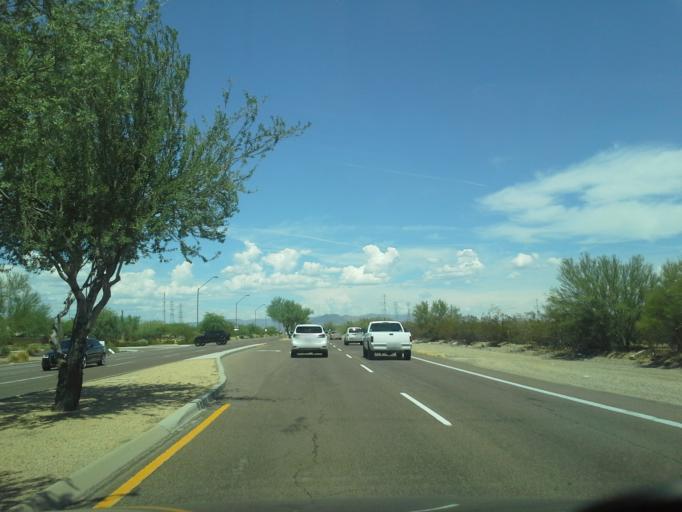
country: US
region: Arizona
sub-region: Maricopa County
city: Cave Creek
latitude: 33.7034
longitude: -112.0230
